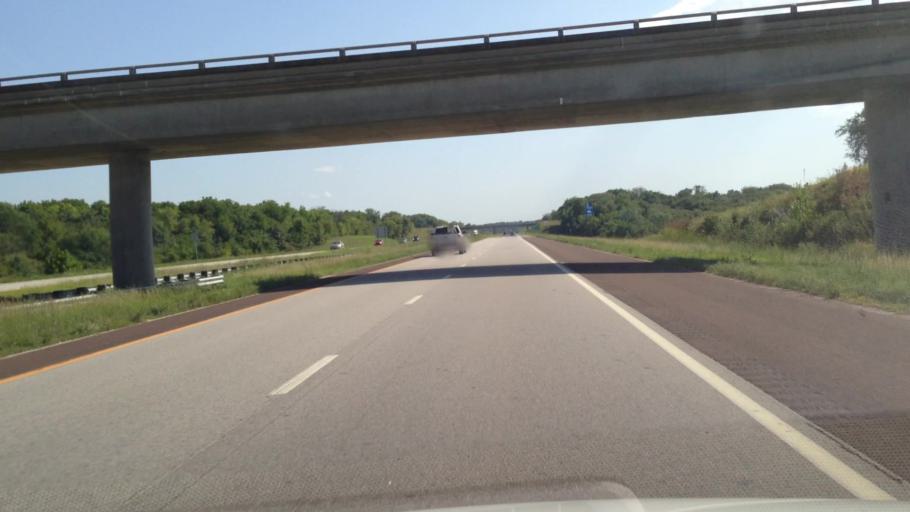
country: US
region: Kansas
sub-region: Miami County
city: Louisburg
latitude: 38.6141
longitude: -94.6949
